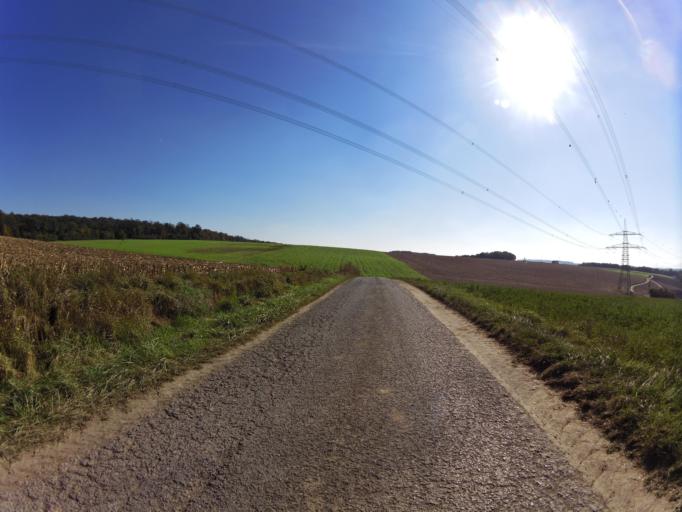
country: DE
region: Bavaria
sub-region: Regierungsbezirk Unterfranken
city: Ochsenfurt
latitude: 49.6854
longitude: 10.0573
